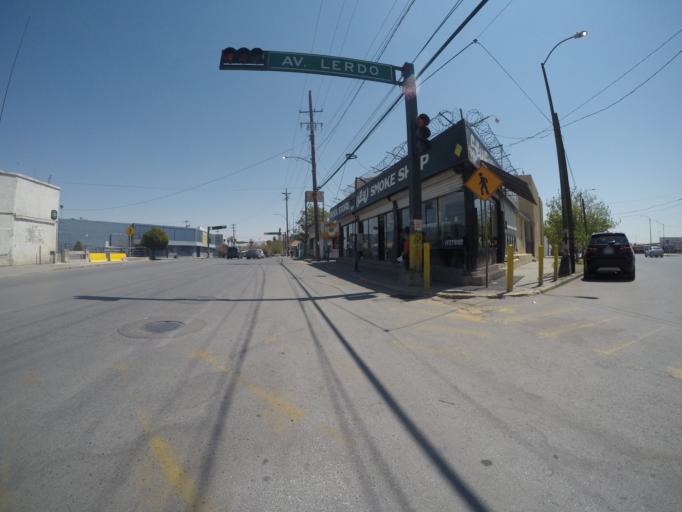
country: MX
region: Chihuahua
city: Ciudad Juarez
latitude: 31.7363
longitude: -106.4815
